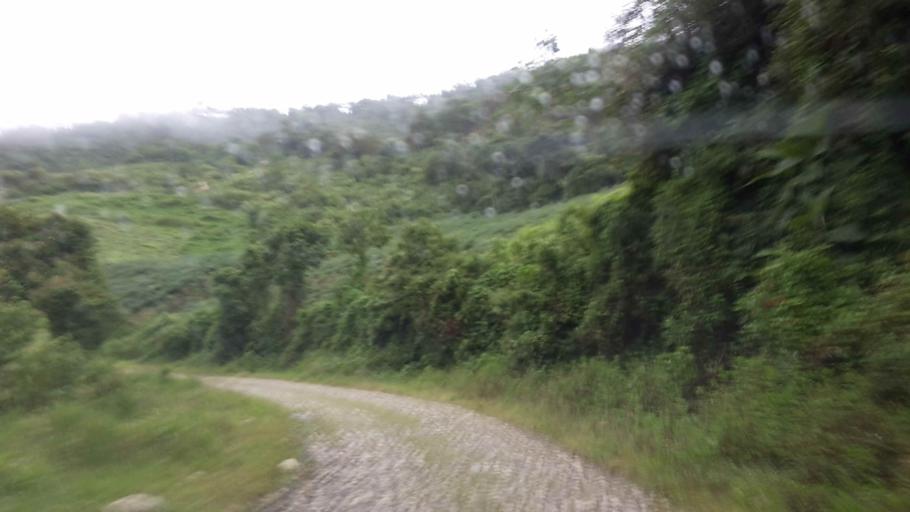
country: BO
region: Cochabamba
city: Colomi
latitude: -17.1312
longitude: -65.9458
